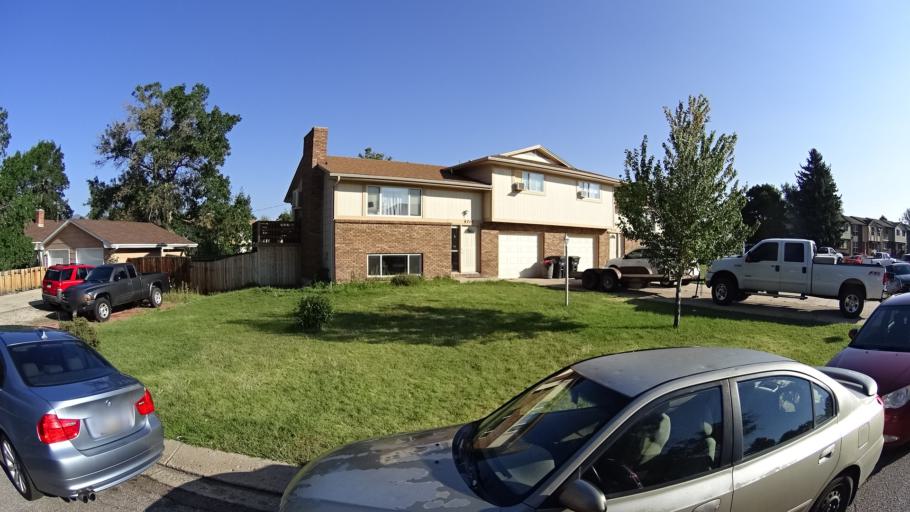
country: US
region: Colorado
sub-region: El Paso County
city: Air Force Academy
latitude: 38.9284
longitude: -104.7978
